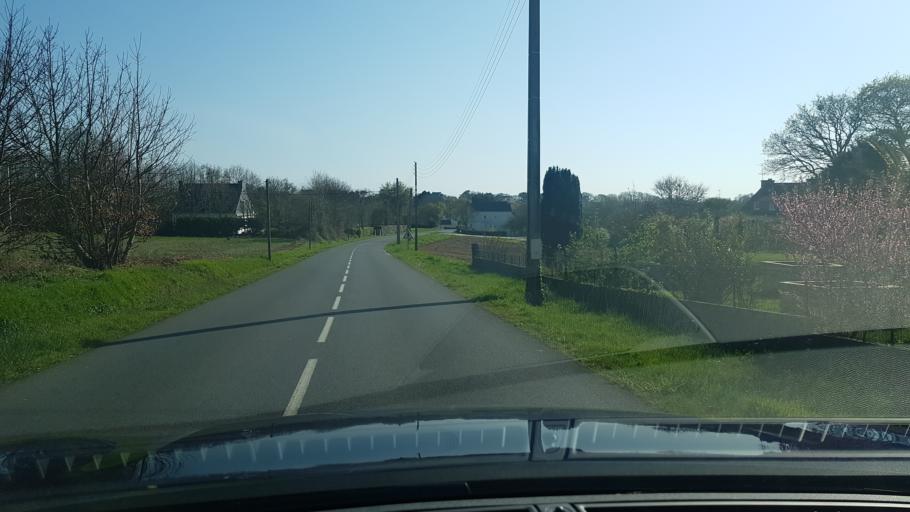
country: FR
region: Brittany
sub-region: Departement du Finistere
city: Clohars-Carnoet
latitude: 47.7806
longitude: -3.5925
